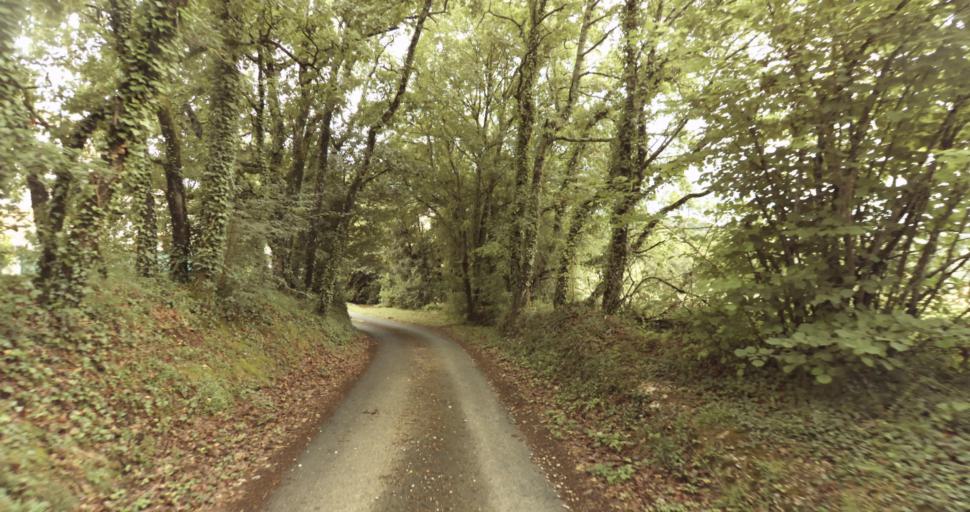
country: FR
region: Aquitaine
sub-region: Departement de la Dordogne
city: Beaumont-du-Perigord
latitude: 44.7584
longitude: 0.7760
